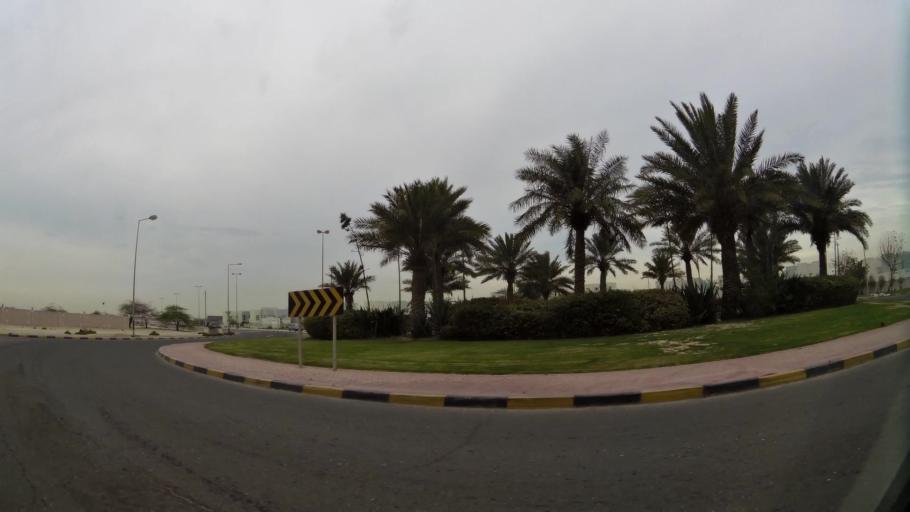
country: BH
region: Northern
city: Ar Rifa'
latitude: 26.0950
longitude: 50.5581
